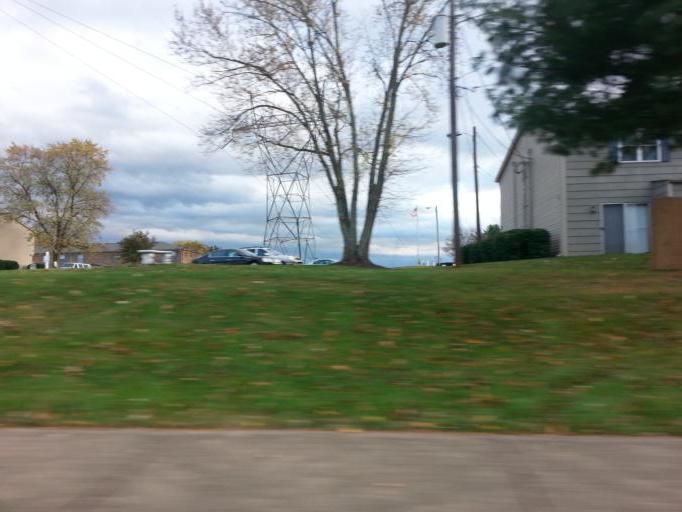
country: US
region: Tennessee
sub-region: Blount County
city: Louisville
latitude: 35.9221
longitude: -84.0358
